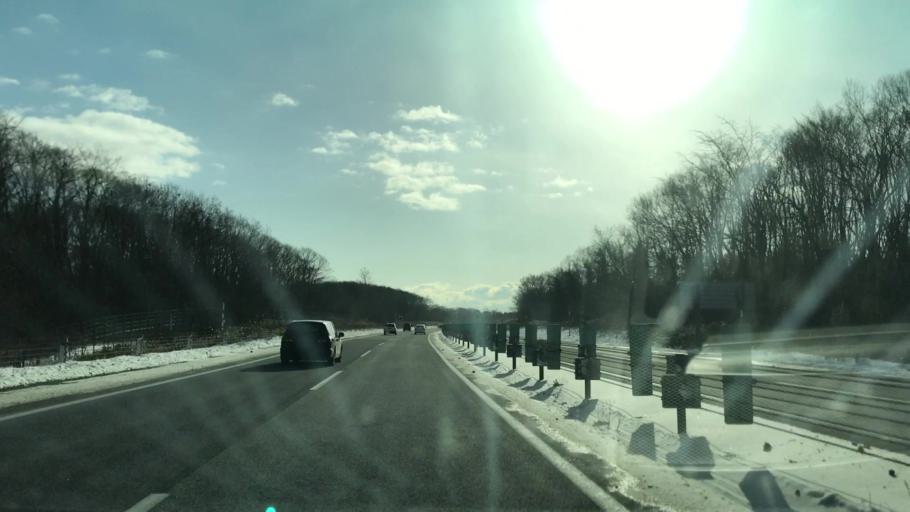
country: JP
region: Hokkaido
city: Chitose
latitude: 42.8346
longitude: 141.6081
